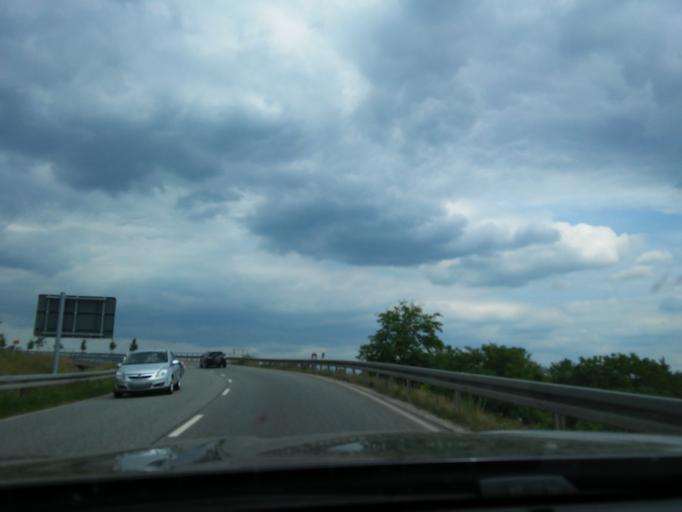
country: DE
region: Thuringia
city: Sondershausen
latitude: 51.3648
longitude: 10.8433
